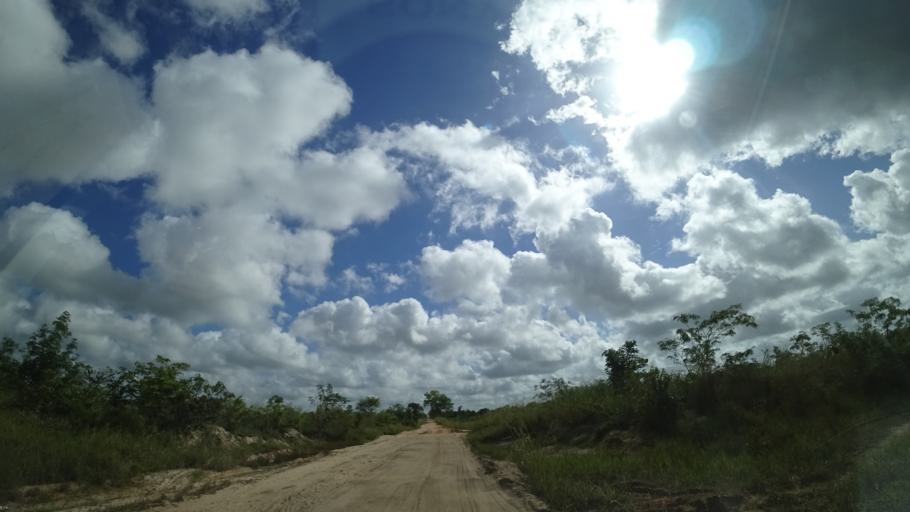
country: MZ
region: Sofala
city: Dondo
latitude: -19.4056
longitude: 34.7094
